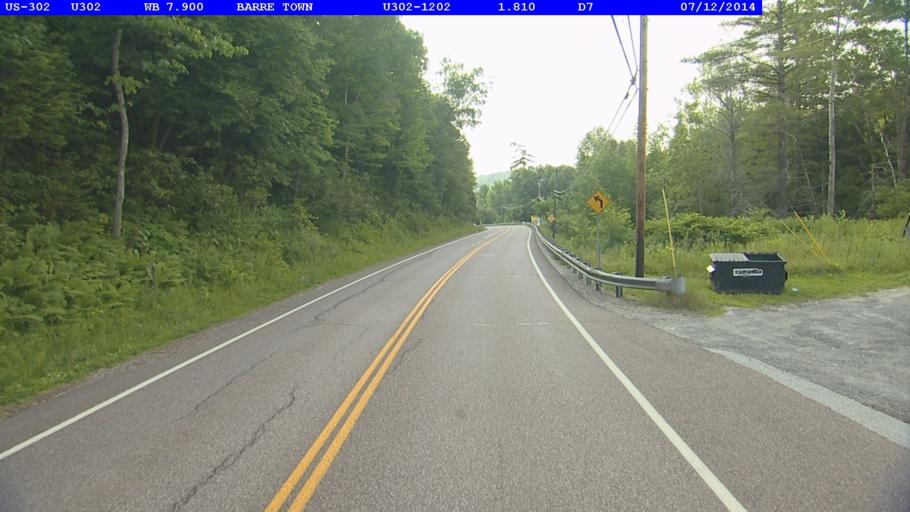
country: US
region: Vermont
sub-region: Washington County
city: South Barre
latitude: 44.1678
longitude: -72.4594
